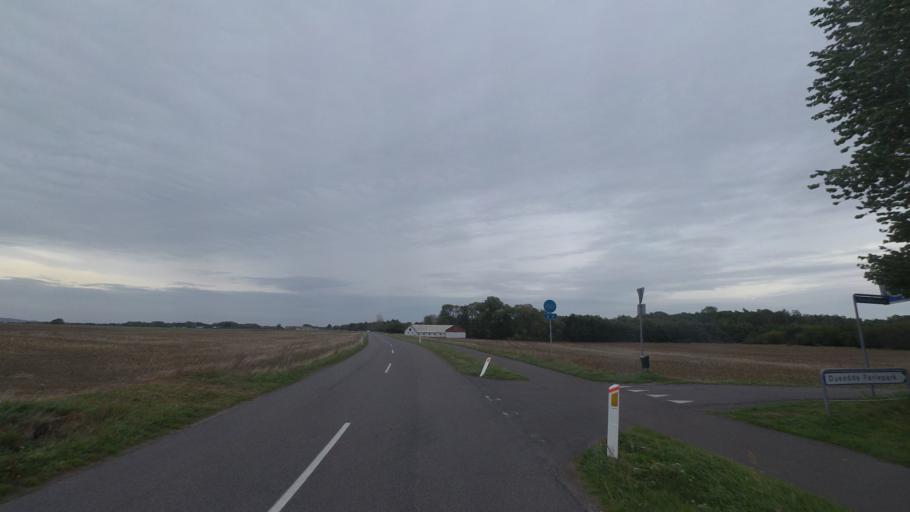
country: DK
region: Capital Region
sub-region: Bornholm Kommune
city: Nexo
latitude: 55.0051
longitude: 15.0878
